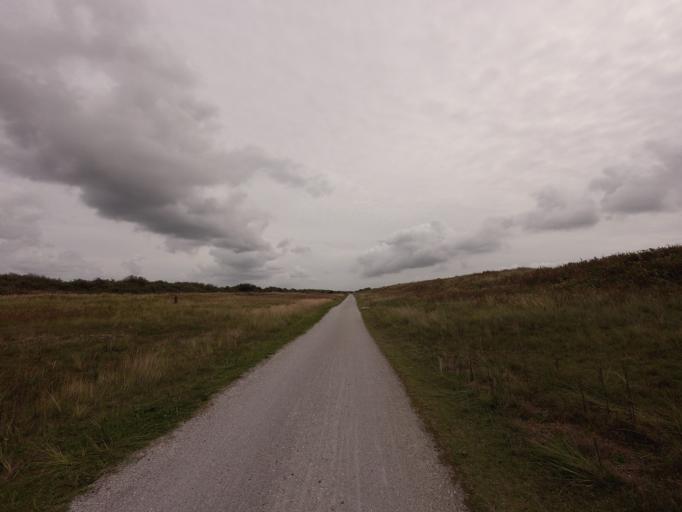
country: NL
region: Friesland
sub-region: Gemeente Ameland
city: Hollum
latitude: 53.4583
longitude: 5.6738
